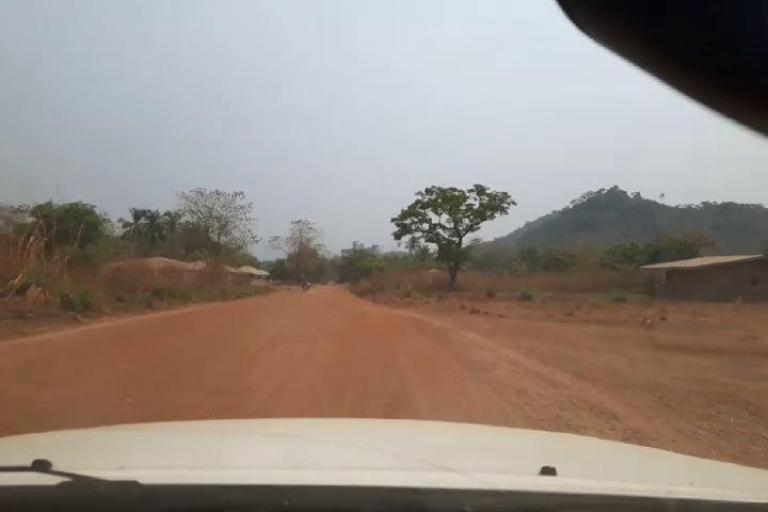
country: SL
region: Northern Province
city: Bumbuna
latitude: 9.0261
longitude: -11.7630
